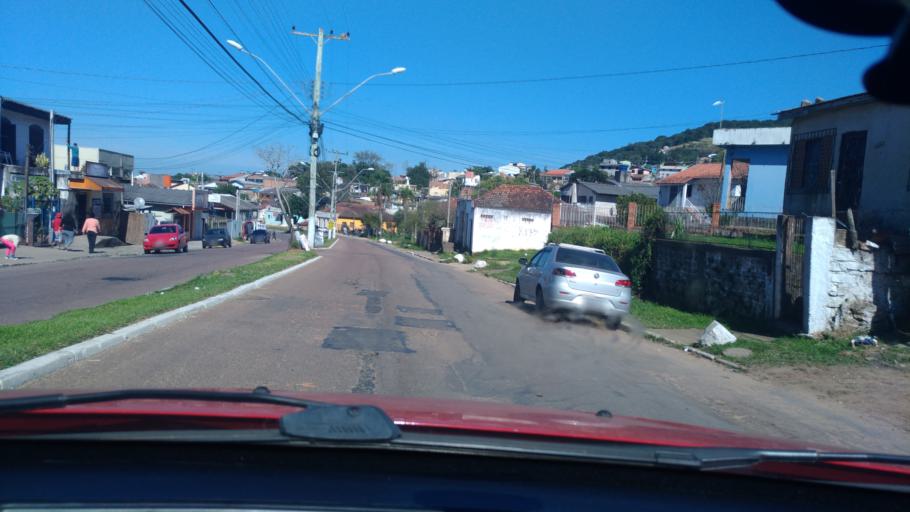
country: BR
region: Rio Grande do Sul
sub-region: Viamao
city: Viamao
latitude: -30.0581
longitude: -51.1078
